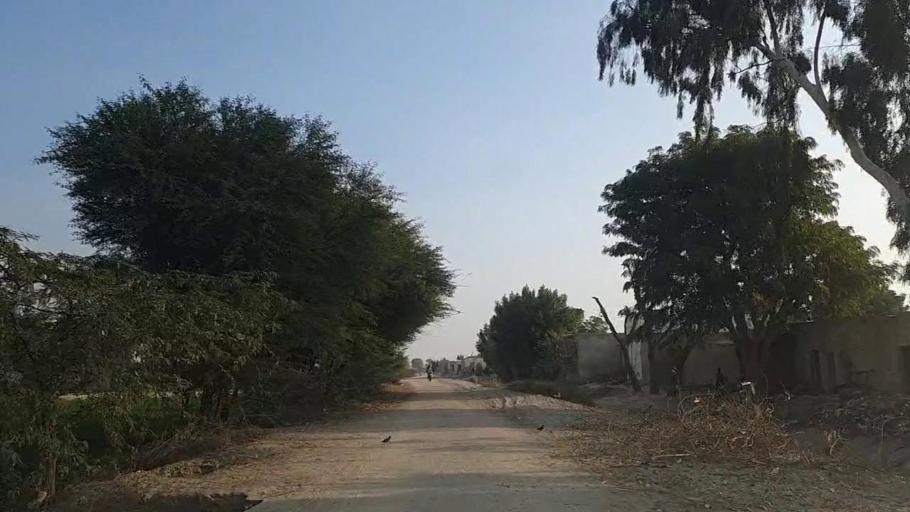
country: PK
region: Sindh
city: Jam Sahib
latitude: 26.4501
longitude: 68.5712
